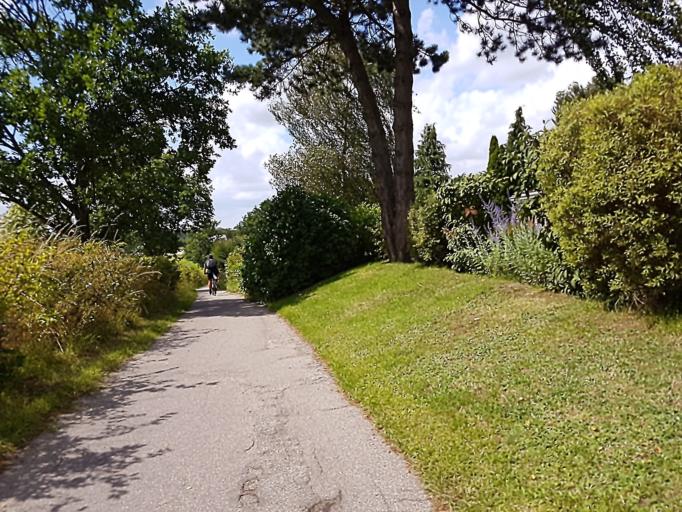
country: DK
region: Capital Region
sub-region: Ballerup Kommune
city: Malov
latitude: 55.7895
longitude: 12.3151
